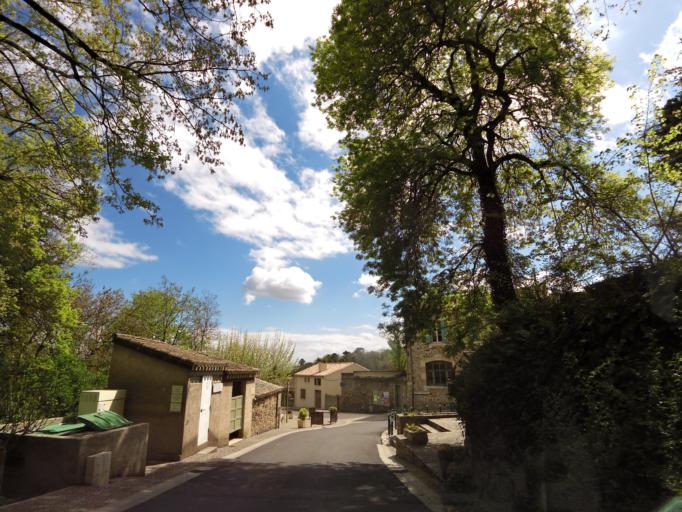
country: FR
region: Languedoc-Roussillon
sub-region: Departement de l'Aude
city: Saint-Martin-Lalande
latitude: 43.3662
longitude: 2.0588
